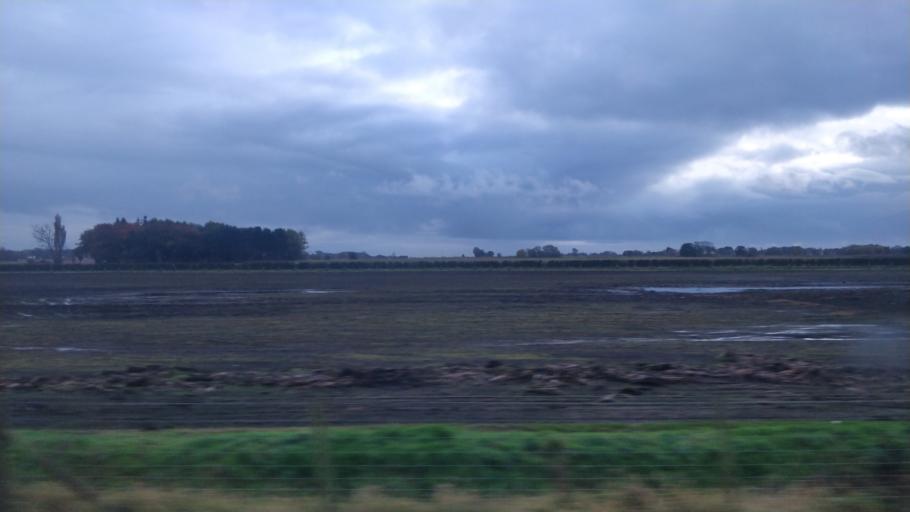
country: GB
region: England
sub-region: Lancashire
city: Banks
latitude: 53.6269
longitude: -2.9257
